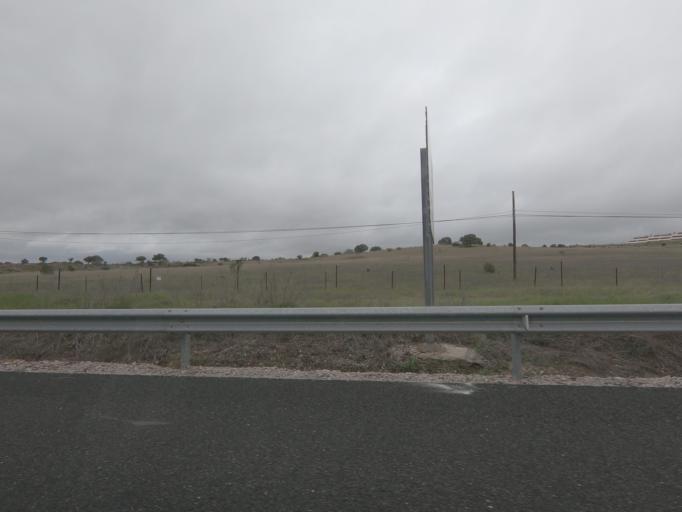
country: ES
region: Extremadura
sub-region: Provincia de Caceres
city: Caceres
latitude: 39.4660
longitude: -6.4059
